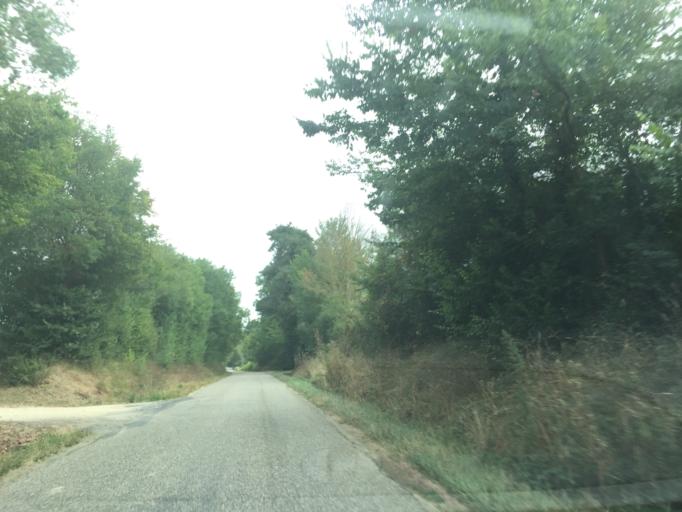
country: FR
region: Midi-Pyrenees
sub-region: Departement du Gers
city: Vic-Fezensac
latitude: 43.6691
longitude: 0.3866
